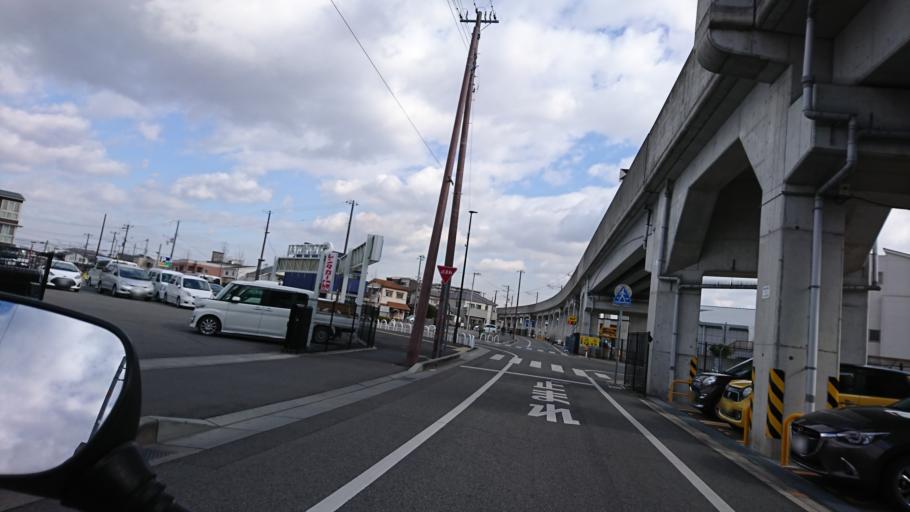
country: JP
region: Hyogo
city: Kakogawacho-honmachi
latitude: 34.7662
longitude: 134.8423
